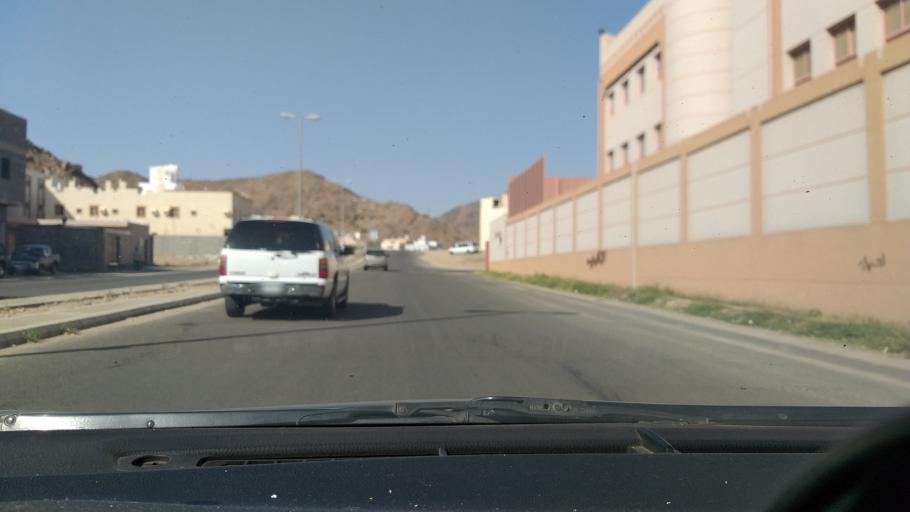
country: SA
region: Makkah
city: Ta'if
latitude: 21.2239
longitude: 40.3742
